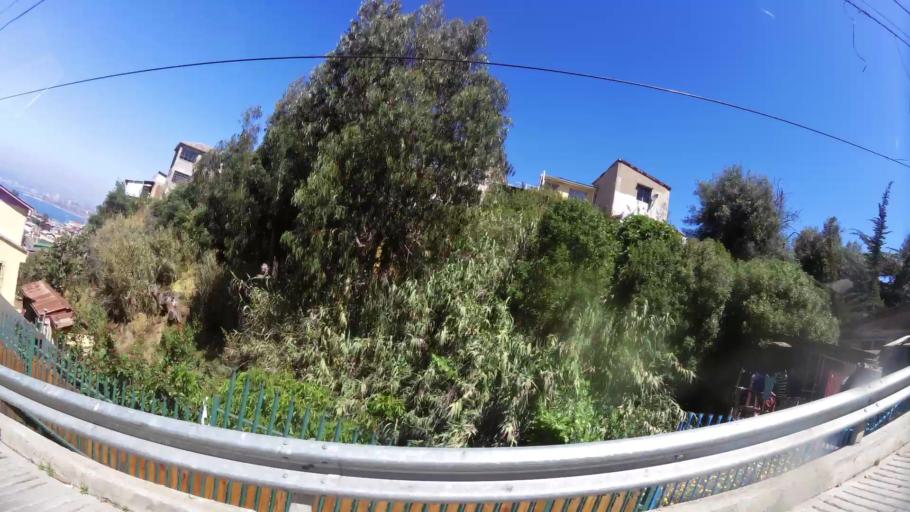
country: CL
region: Valparaiso
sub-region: Provincia de Valparaiso
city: Valparaiso
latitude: -33.0334
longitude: -71.6391
